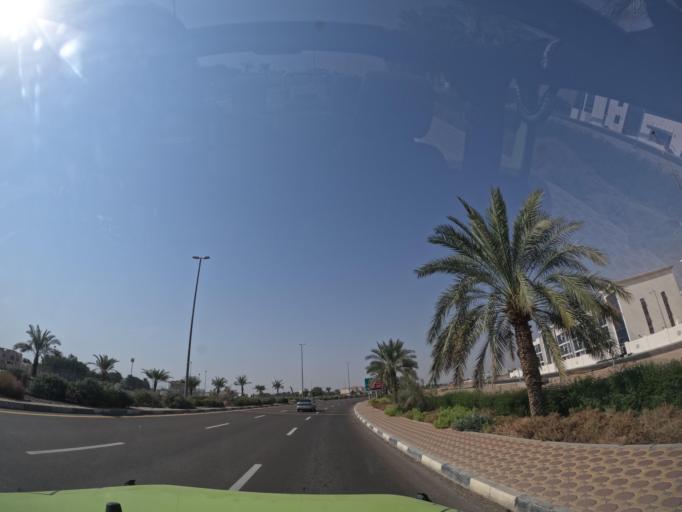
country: AE
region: Abu Dhabi
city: Al Ain
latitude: 24.2578
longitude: 55.6939
